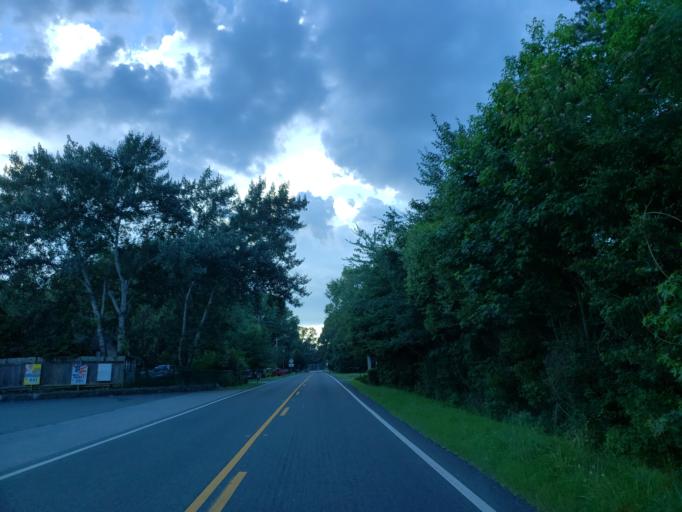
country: US
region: Georgia
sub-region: Bartow County
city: Cartersville
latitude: 34.2002
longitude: -84.7408
